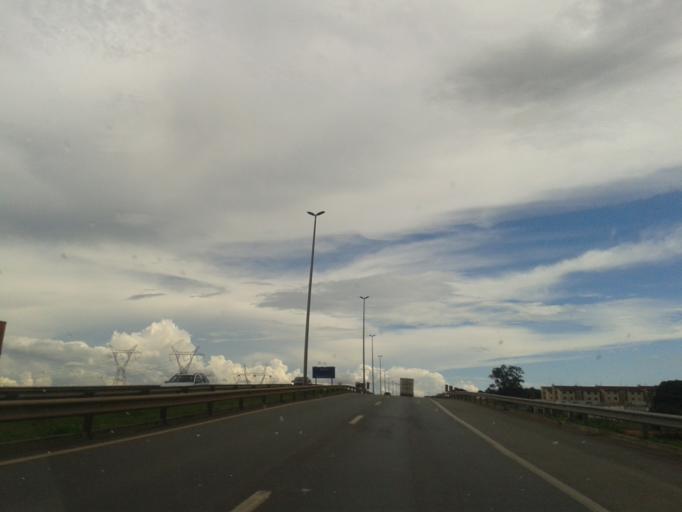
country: BR
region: Goias
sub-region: Aparecida De Goiania
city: Aparecida de Goiania
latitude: -16.8171
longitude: -49.2404
